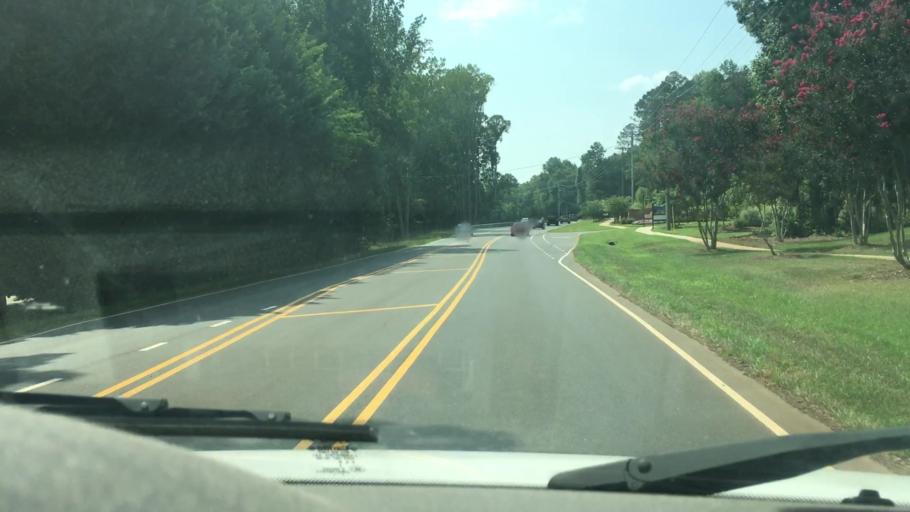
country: US
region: North Carolina
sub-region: Mecklenburg County
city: Huntersville
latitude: 35.4055
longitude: -80.8837
